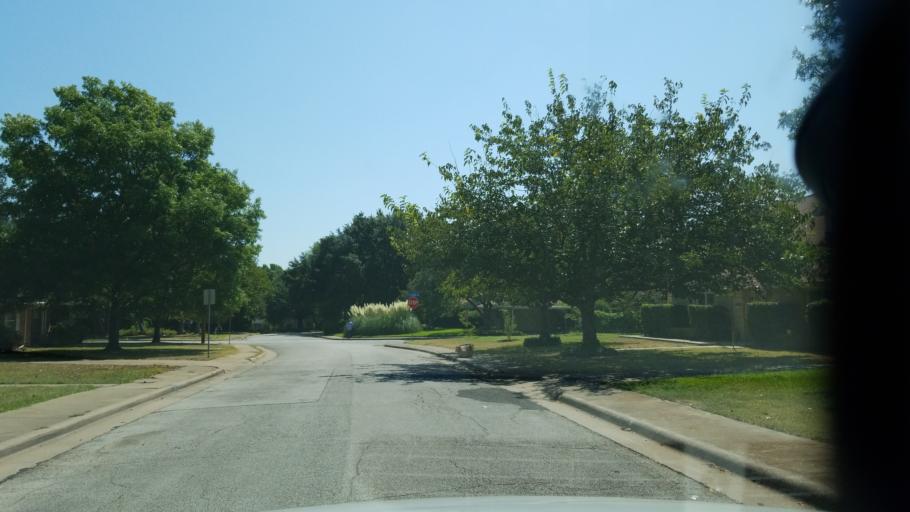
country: US
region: Texas
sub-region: Dallas County
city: Duncanville
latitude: 32.6445
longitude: -96.8968
